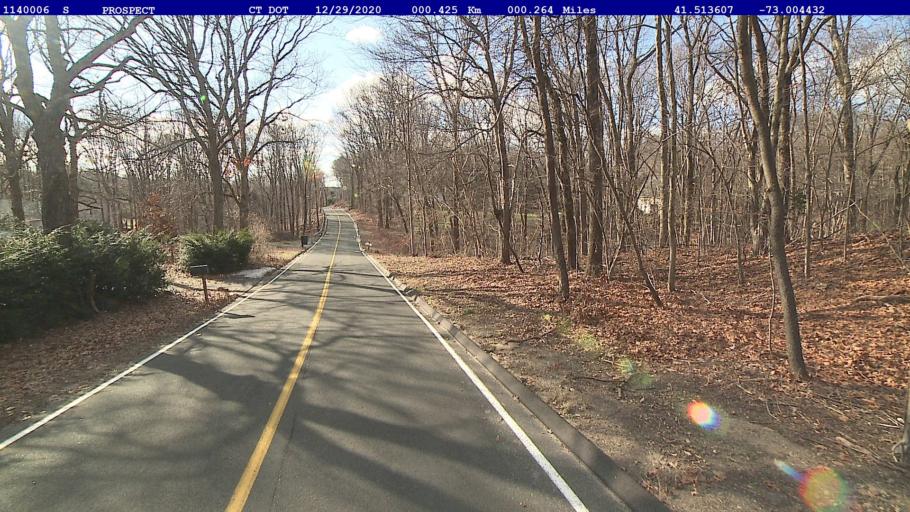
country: US
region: Connecticut
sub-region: New Haven County
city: Prospect
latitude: 41.5136
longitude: -73.0044
